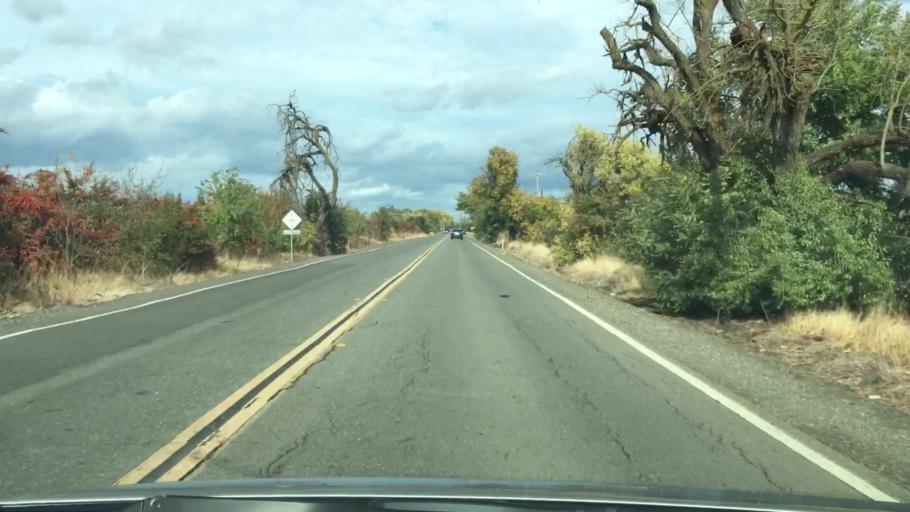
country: US
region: California
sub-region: Yolo County
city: Davis
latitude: 38.5409
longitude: -121.8033
